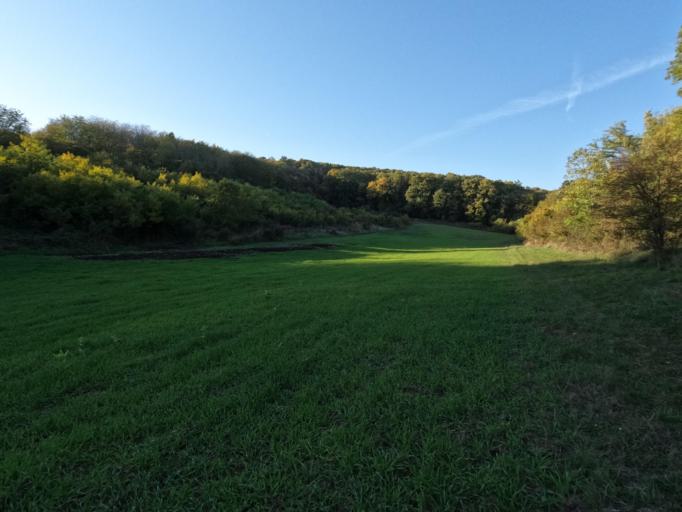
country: HU
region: Tolna
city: Szekszard
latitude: 46.3062
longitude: 18.6554
